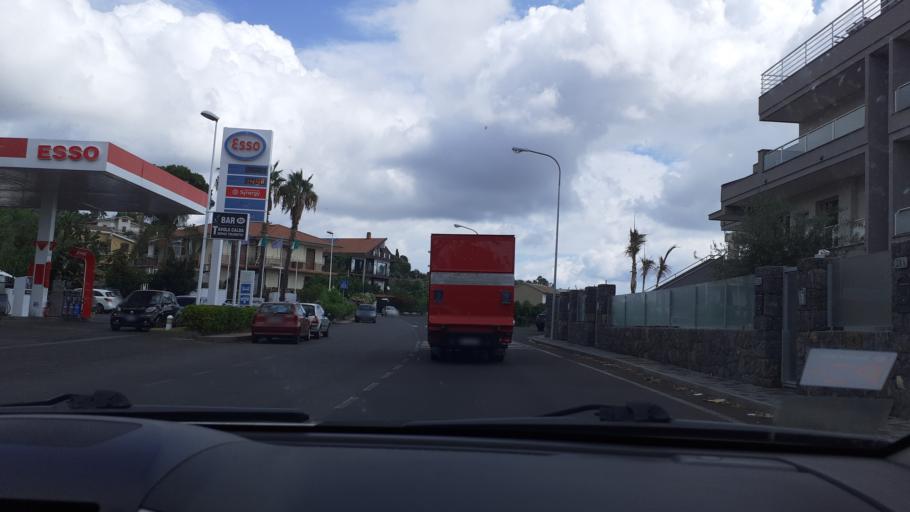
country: IT
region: Sicily
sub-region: Catania
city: Cerza
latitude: 37.5498
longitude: 15.1005
